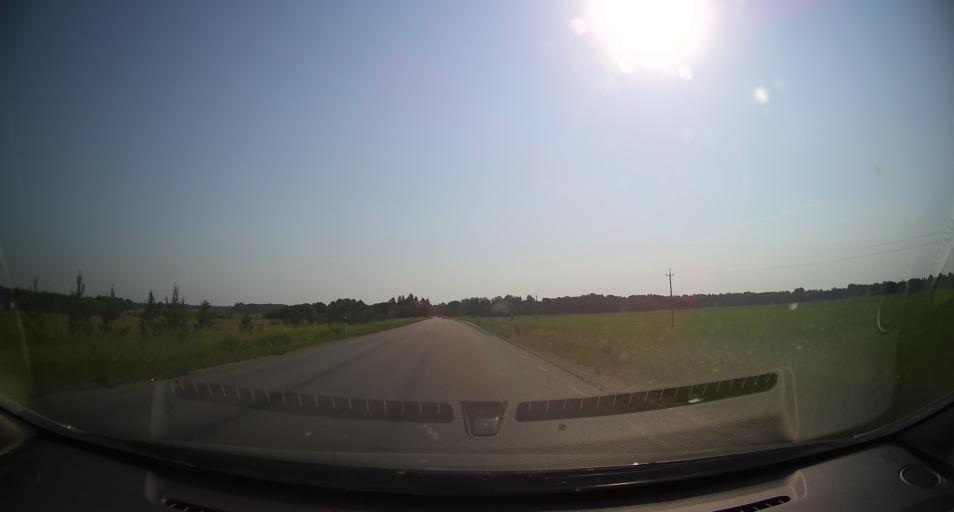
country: EE
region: Harju
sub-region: Rae vald
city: Vaida
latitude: 59.3606
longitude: 24.9877
